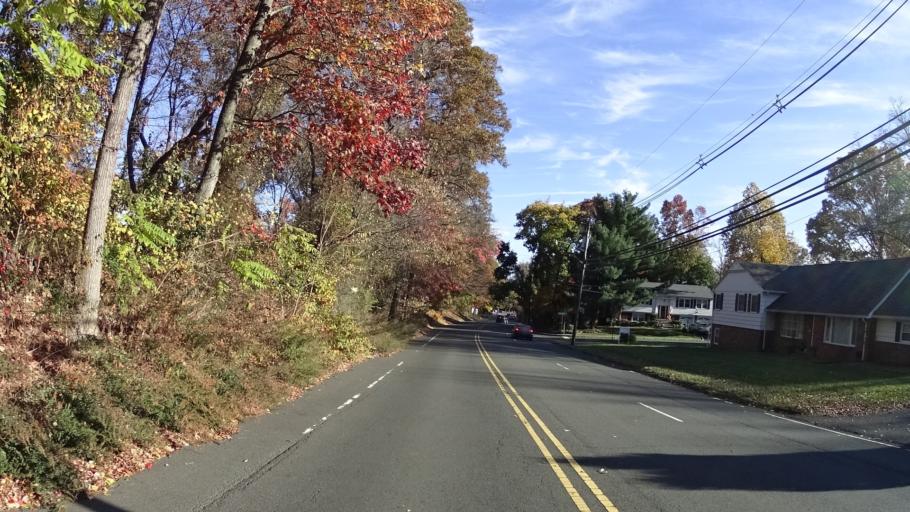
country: US
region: New Jersey
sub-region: Union County
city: Mountainside
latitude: 40.6735
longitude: -74.3600
